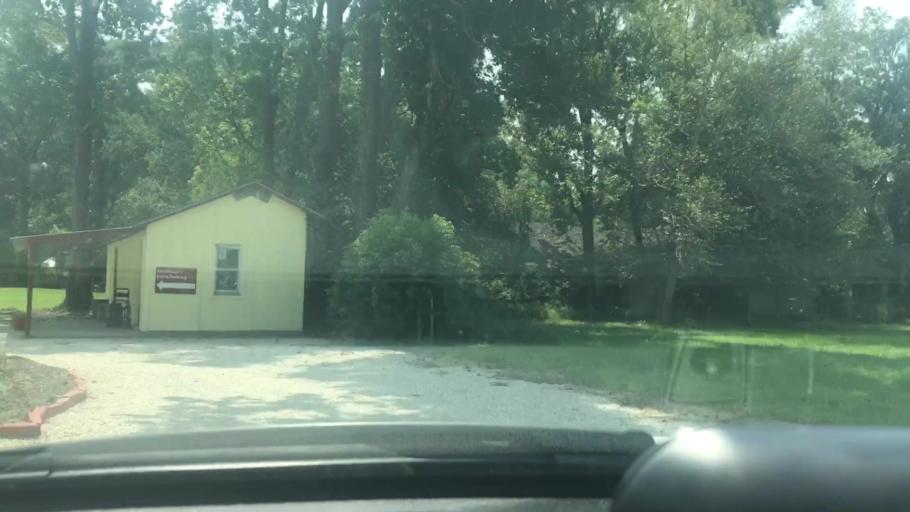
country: US
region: Louisiana
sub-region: Livingston Parish
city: Denham Springs
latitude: 30.4765
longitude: -90.9591
